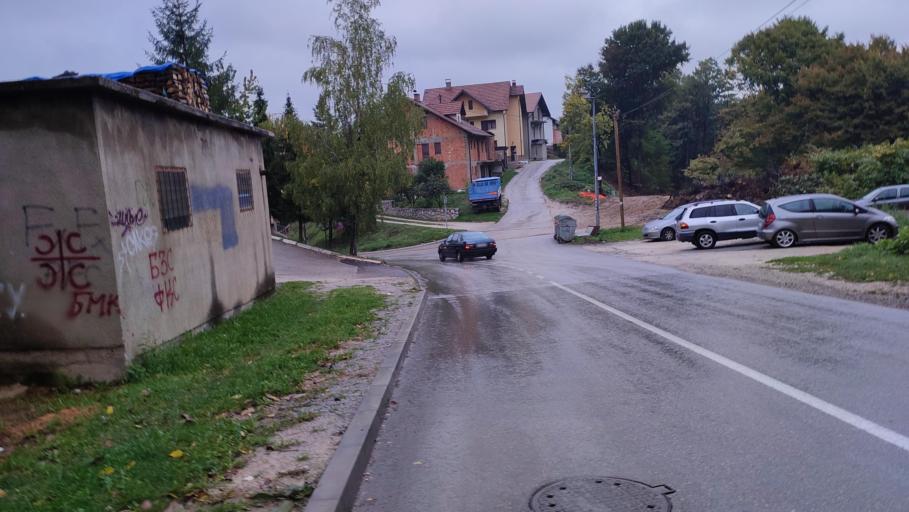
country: RS
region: Central Serbia
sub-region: Zlatiborski Okrug
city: Uzice
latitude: 43.8590
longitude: 19.8570
